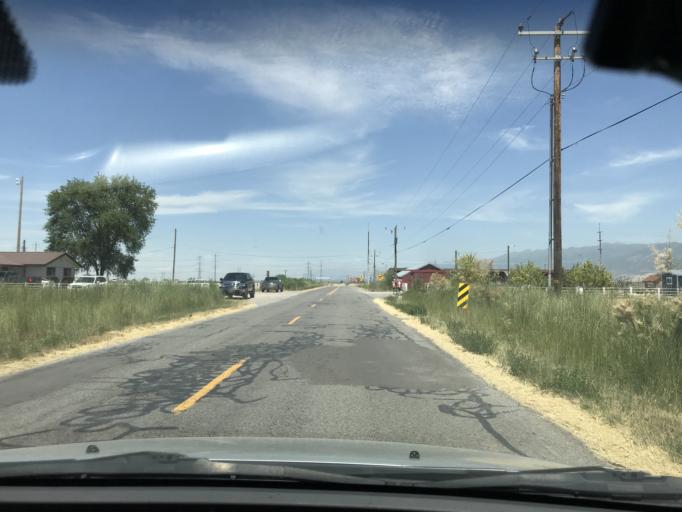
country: US
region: Utah
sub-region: Davis County
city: North Salt Lake
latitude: 40.8402
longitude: -111.9551
